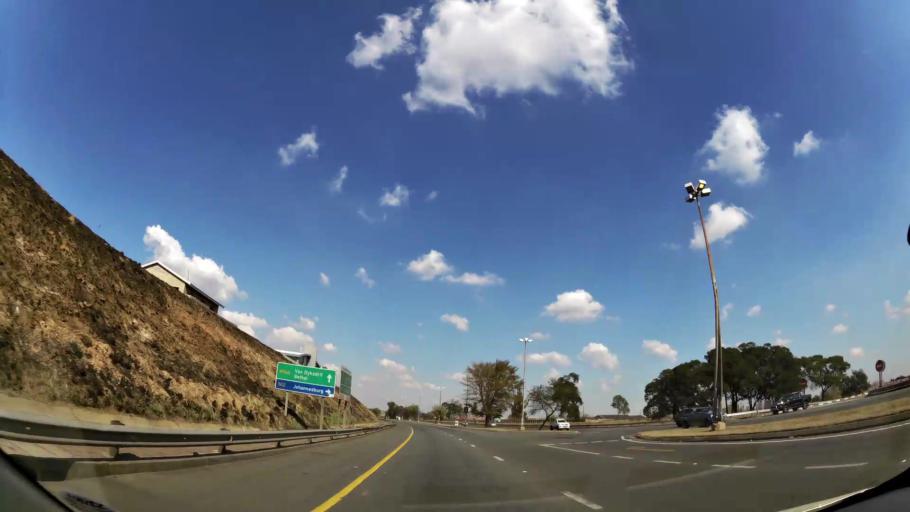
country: ZA
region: Mpumalanga
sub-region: Nkangala District Municipality
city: Witbank
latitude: -25.9197
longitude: 29.2335
